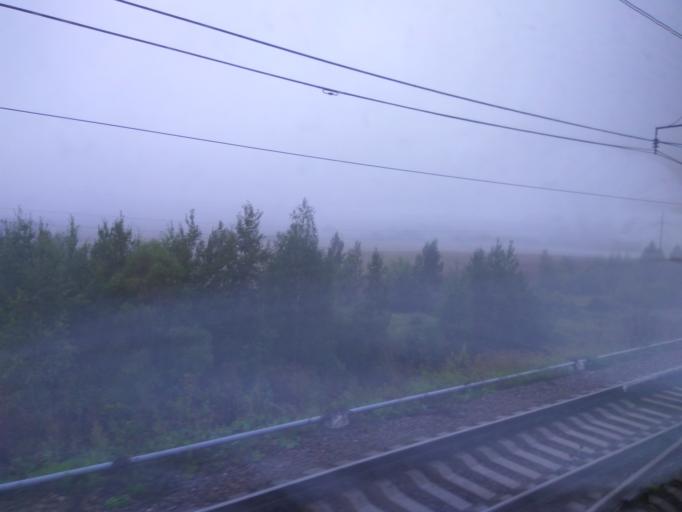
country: RU
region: Moskovskaya
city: Uzunovo
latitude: 54.5562
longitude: 38.6202
